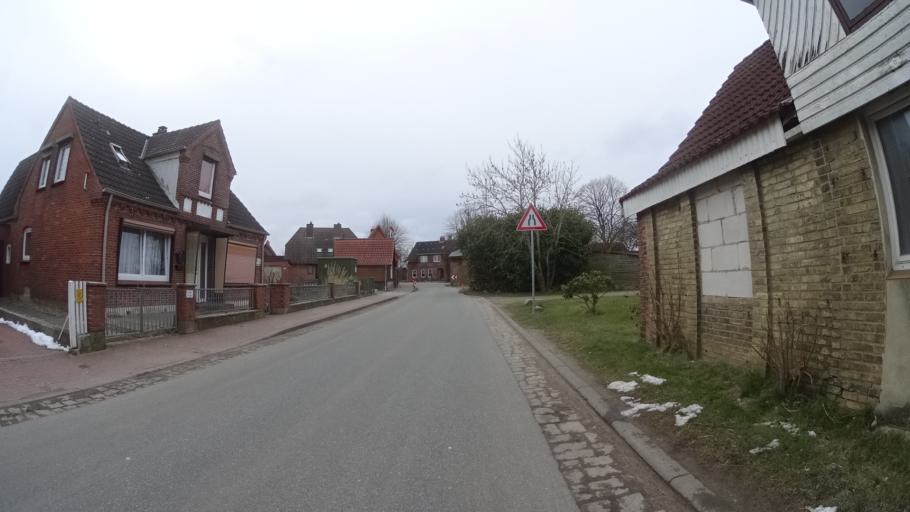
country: DE
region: Schleswig-Holstein
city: Stakendorf
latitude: 54.3898
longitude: 10.4207
